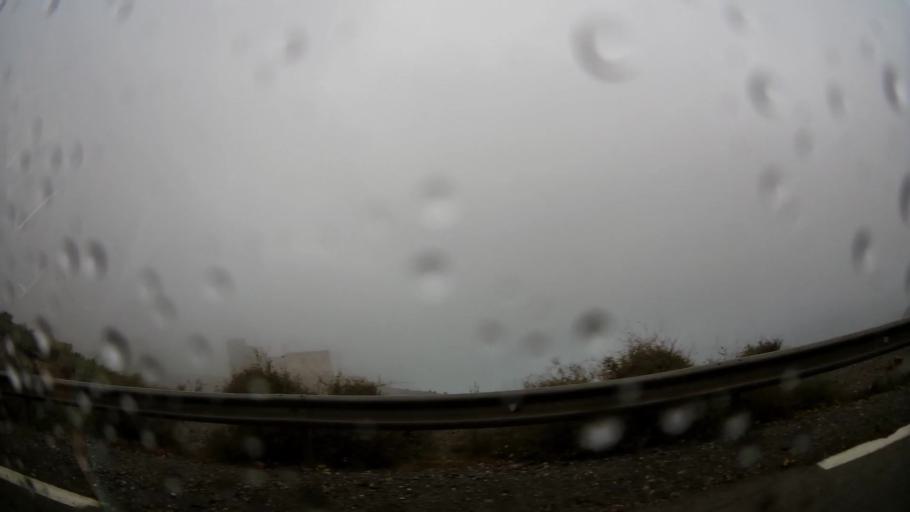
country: MA
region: Taza-Al Hoceima-Taounate
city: Tirhanimine
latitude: 35.2342
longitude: -3.9720
